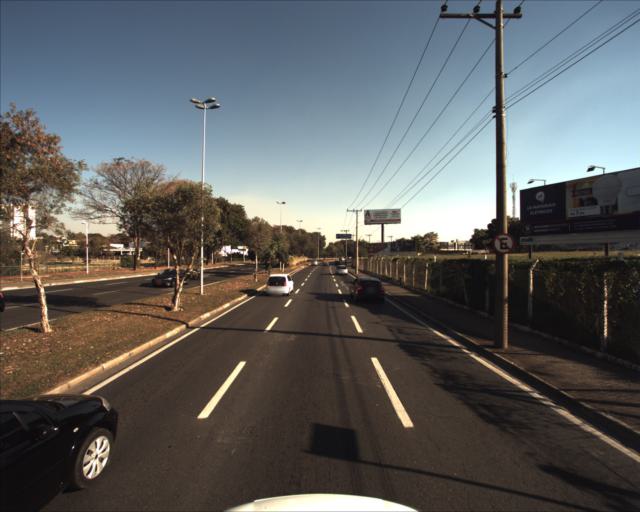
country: BR
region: Sao Paulo
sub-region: Sorocaba
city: Sorocaba
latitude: -23.4880
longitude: -47.4388
